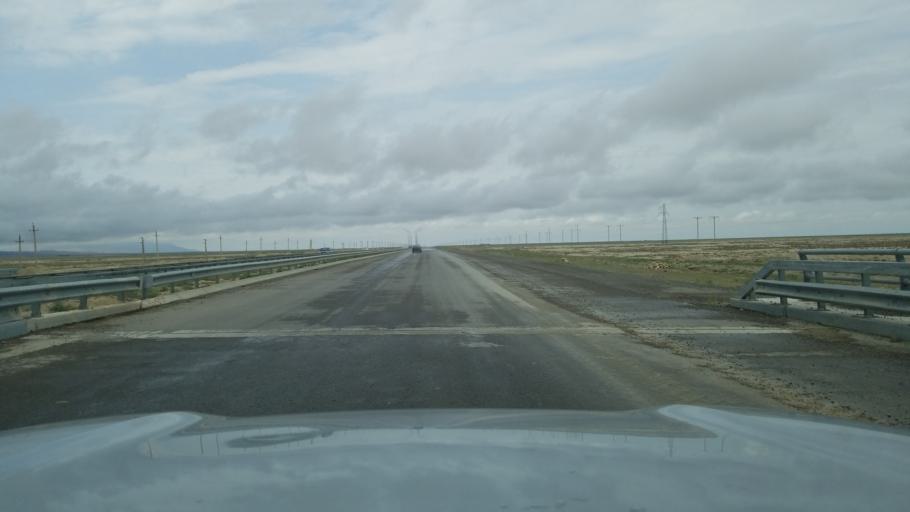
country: TM
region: Balkan
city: Serdar
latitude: 39.1243
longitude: 55.9008
